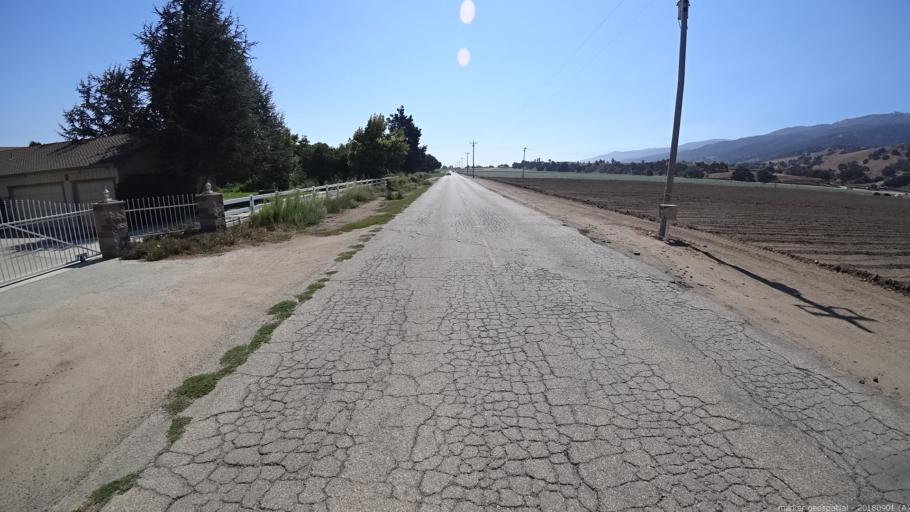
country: US
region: California
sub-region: Monterey County
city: Chualar
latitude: 36.5309
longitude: -121.5324
